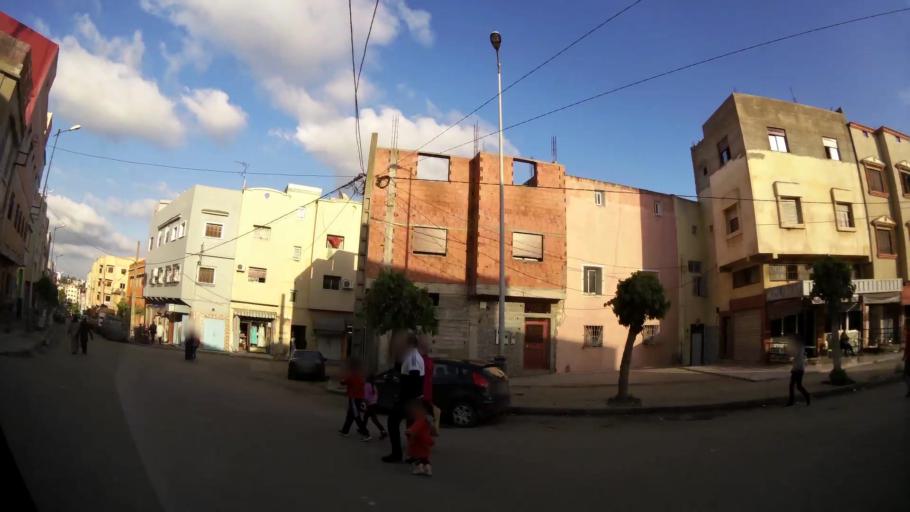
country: MA
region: Chaouia-Ouardigha
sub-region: Settat Province
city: Settat
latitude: 33.0037
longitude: -7.6245
